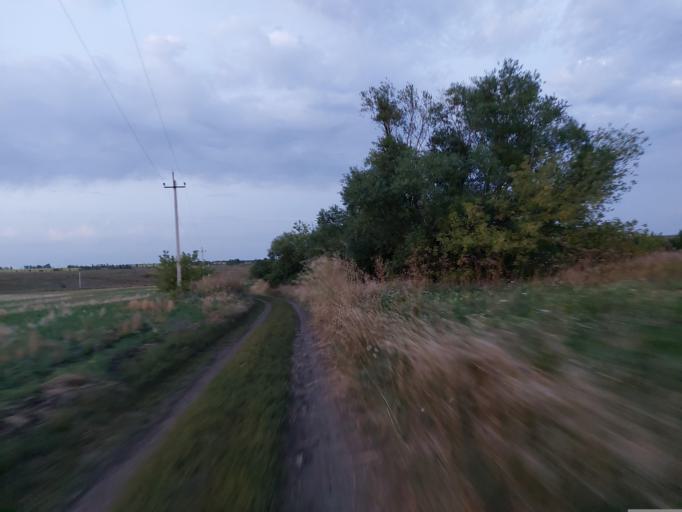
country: RU
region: Lipetsk
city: Dolgorukovo
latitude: 52.3828
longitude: 38.0475
